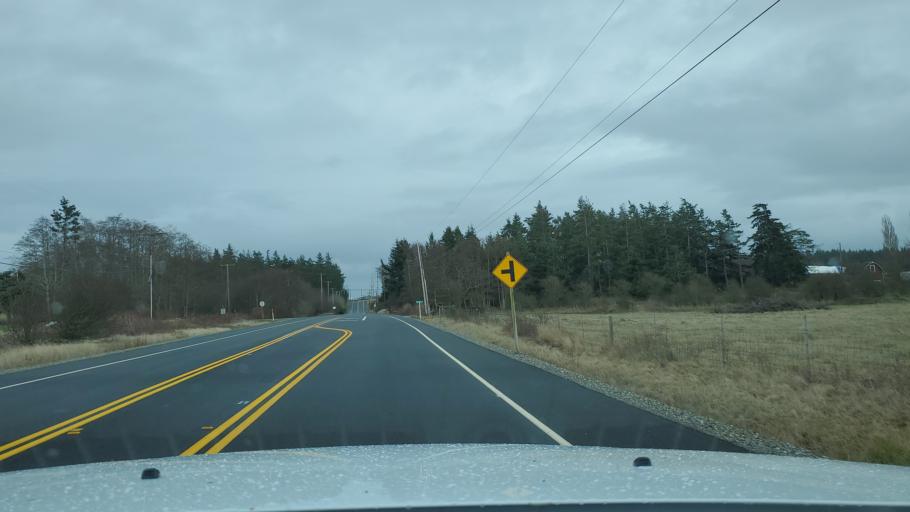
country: US
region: Washington
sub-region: Island County
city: Ault Field
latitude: 48.3260
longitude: -122.6816
